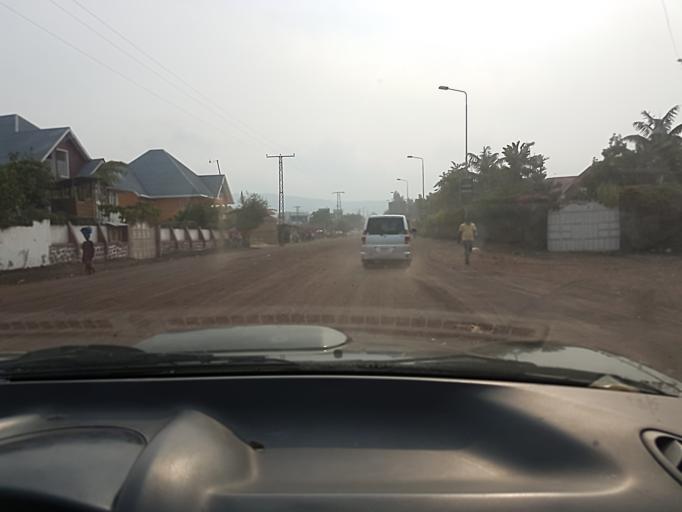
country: CD
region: Nord Kivu
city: Goma
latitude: -1.6882
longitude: 29.2343
